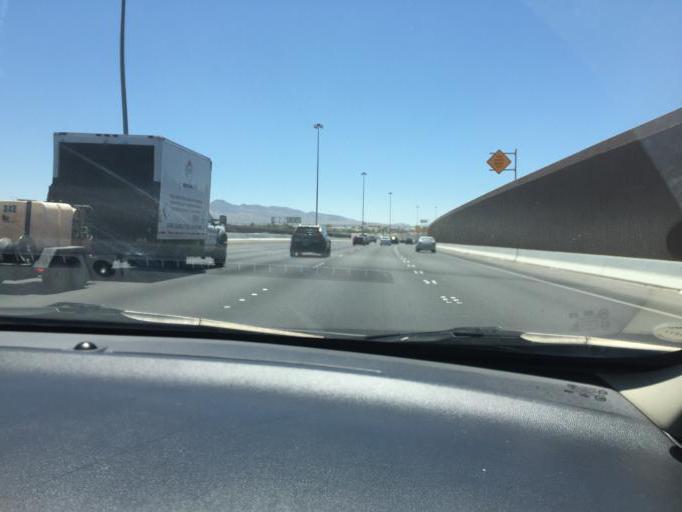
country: US
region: Nevada
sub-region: Clark County
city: Paradise
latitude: 36.0491
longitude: -115.1355
